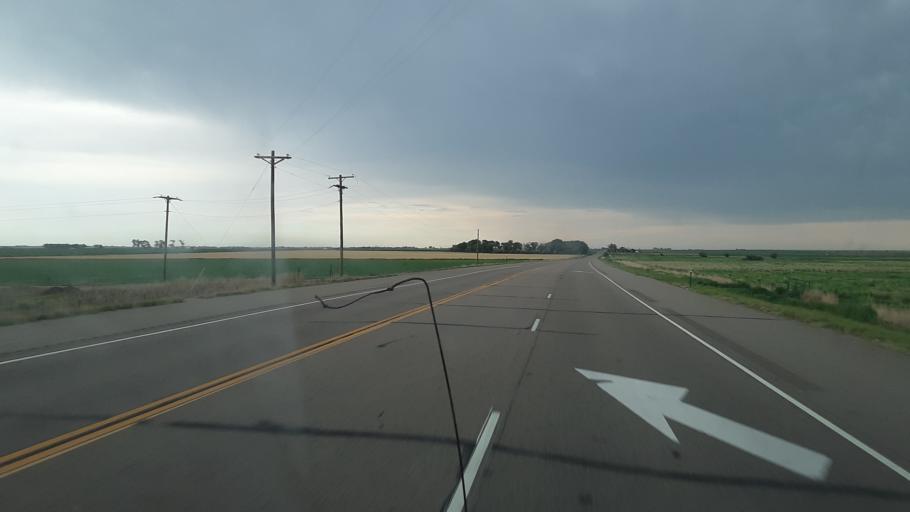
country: US
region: Colorado
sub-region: Bent County
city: Las Animas
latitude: 38.1140
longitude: -102.9373
